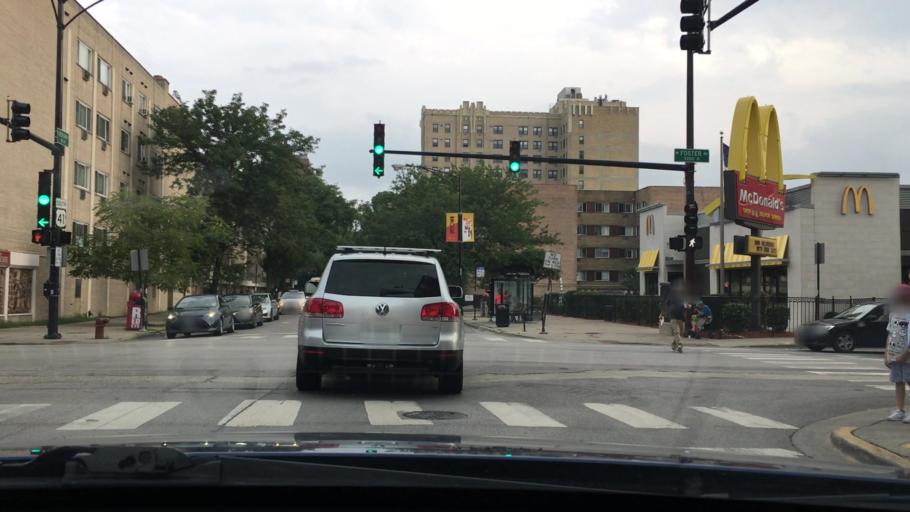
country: US
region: Illinois
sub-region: Cook County
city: Evanston
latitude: 41.9766
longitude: -87.6551
